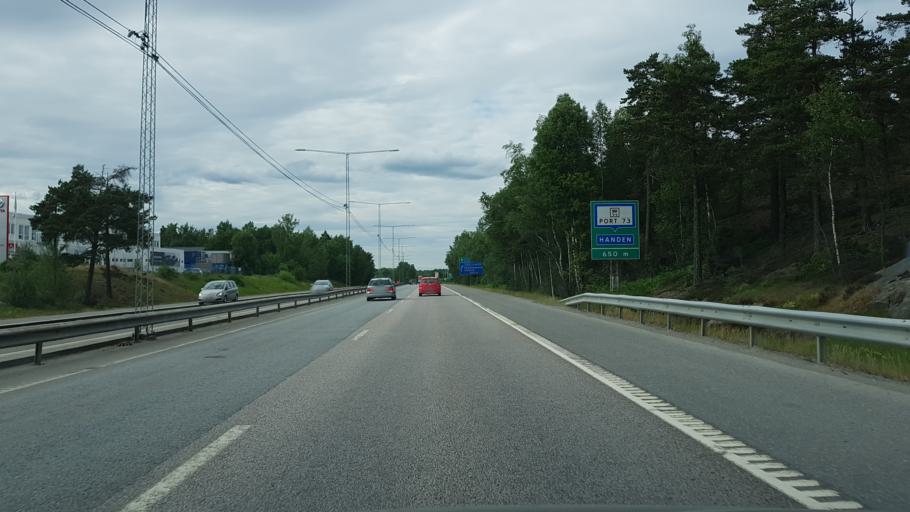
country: SE
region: Stockholm
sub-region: Haninge Kommun
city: Haninge
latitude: 59.1704
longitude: 18.1591
